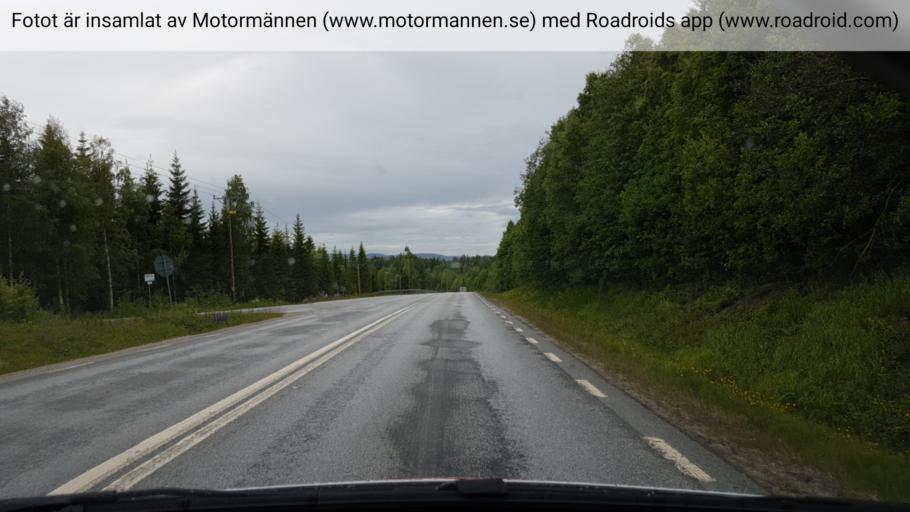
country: SE
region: Vaesterbotten
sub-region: Bjurholms Kommun
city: Bjurholm
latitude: 63.9303
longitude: 19.2638
